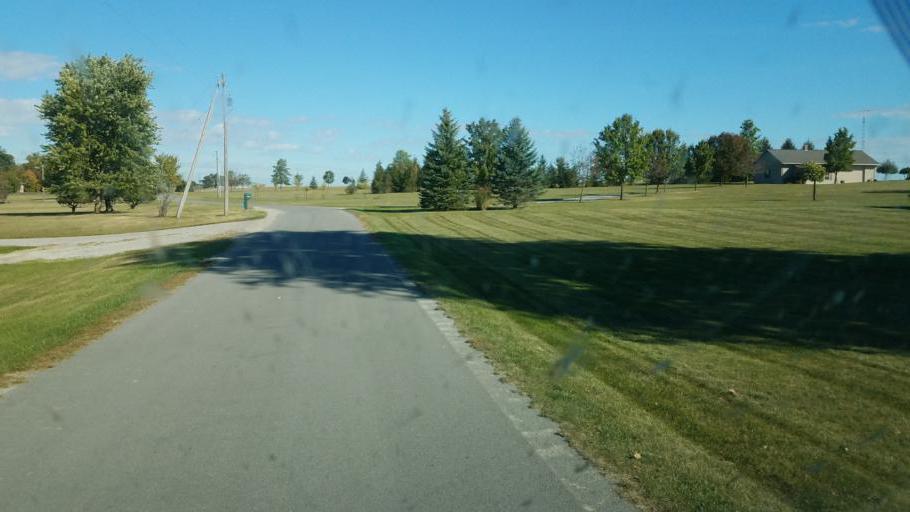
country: US
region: Ohio
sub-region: Wyandot County
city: Upper Sandusky
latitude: 40.7903
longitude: -83.2322
